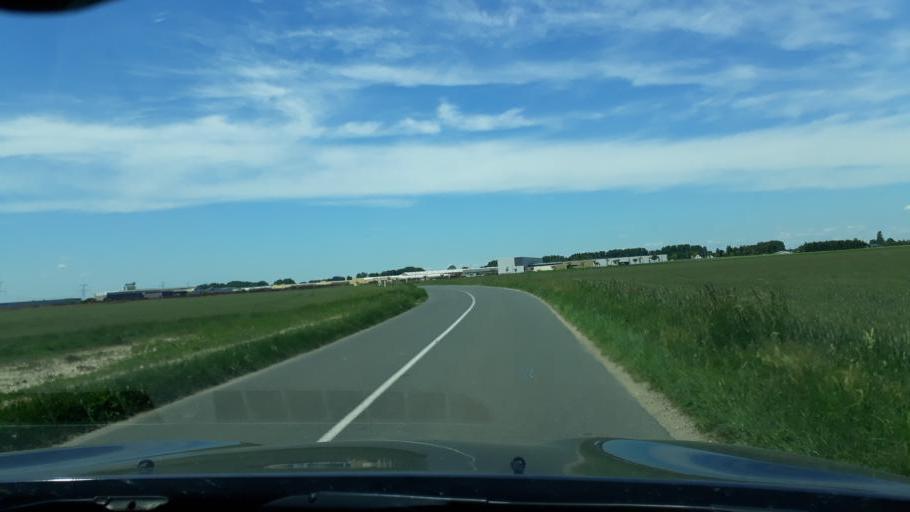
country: FR
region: Centre
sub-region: Departement du Loiret
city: Pithiviers-le-Vieil
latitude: 48.1237
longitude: 2.2034
